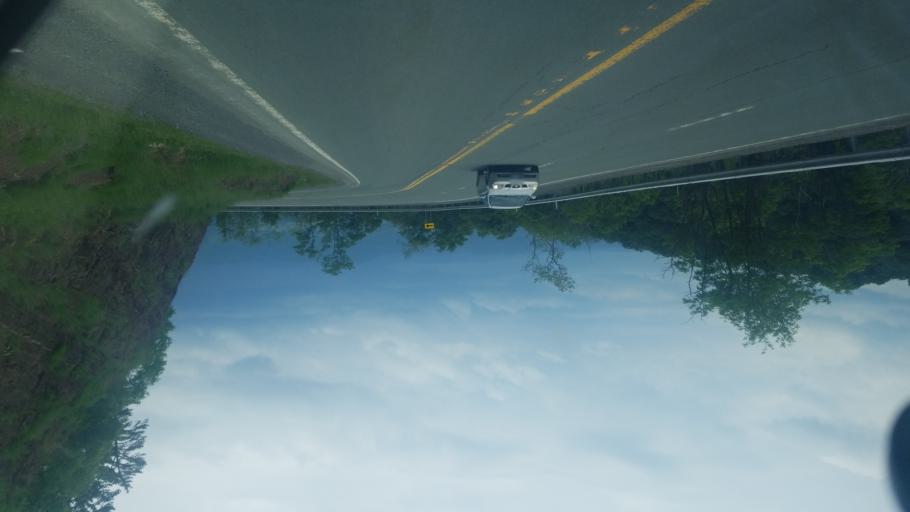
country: US
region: West Virginia
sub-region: Pendleton County
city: Franklin
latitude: 38.5885
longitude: -79.1694
